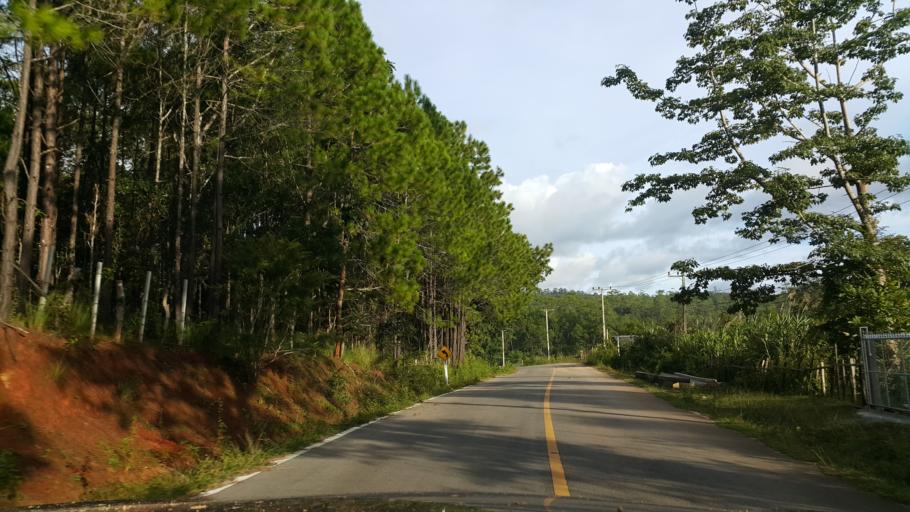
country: TH
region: Chiang Mai
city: Chaem Luang
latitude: 19.0805
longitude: 98.3303
